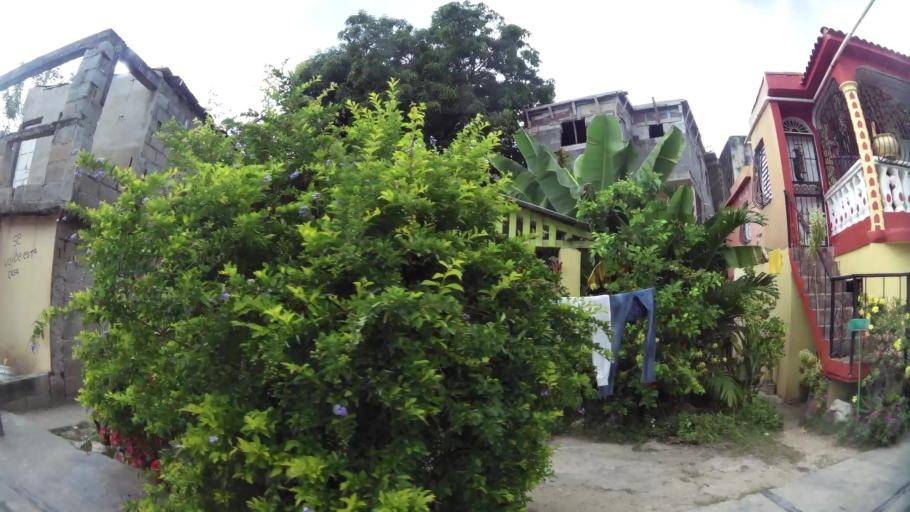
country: DO
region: San Cristobal
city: San Cristobal
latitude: 18.4208
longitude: -70.0896
